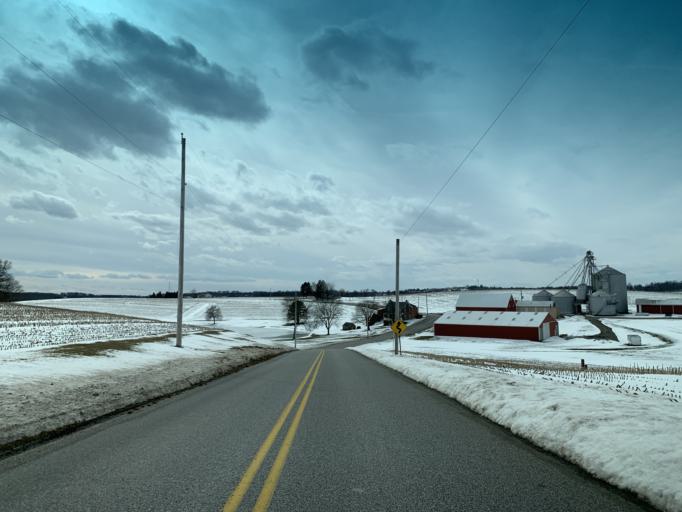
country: US
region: Pennsylvania
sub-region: York County
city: Shrewsbury
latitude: 39.7804
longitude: -76.6436
